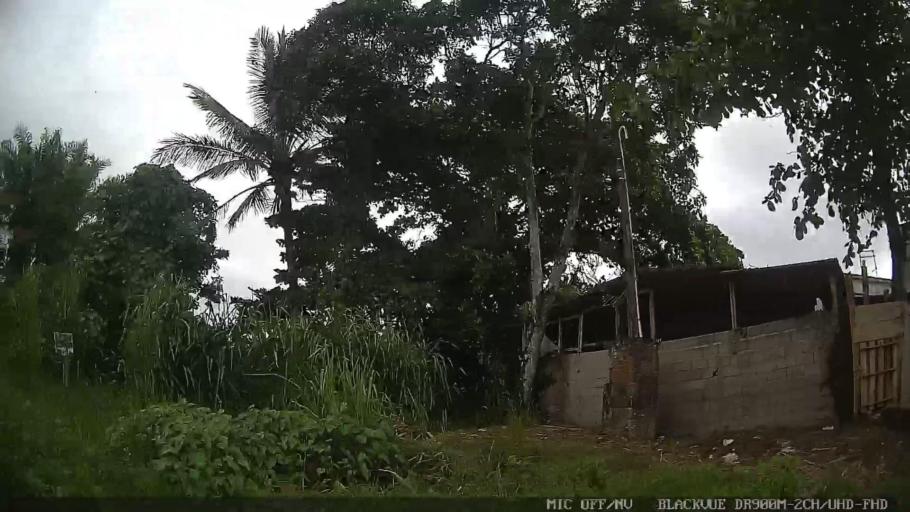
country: BR
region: Sao Paulo
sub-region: Itanhaem
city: Itanhaem
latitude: -24.2141
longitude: -46.8617
